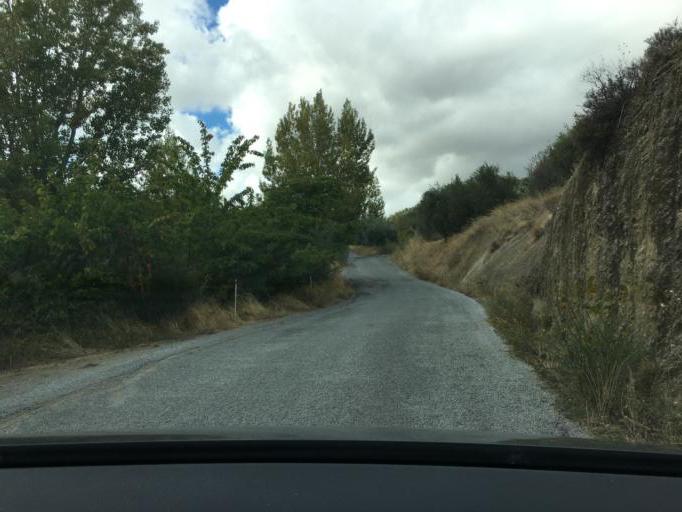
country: ES
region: Andalusia
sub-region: Provincia de Granada
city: Quentar
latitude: 37.1986
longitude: -3.4660
